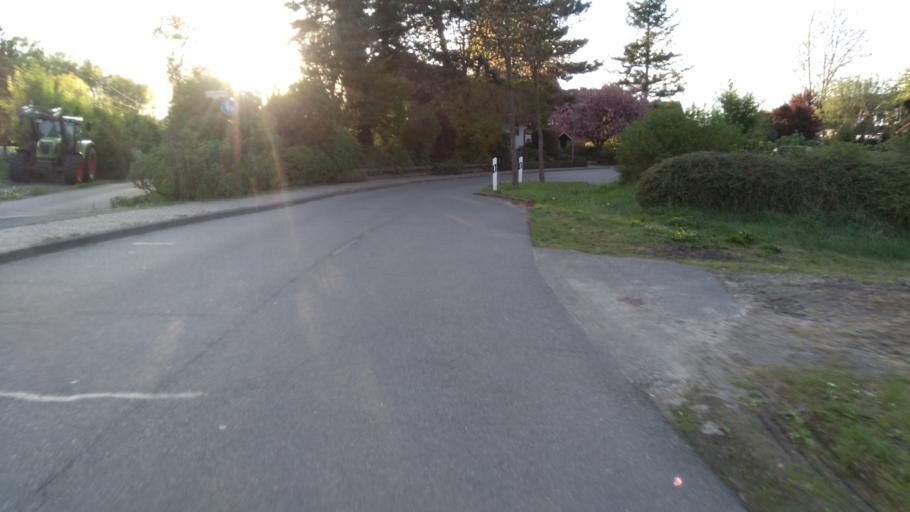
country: DE
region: Lower Saxony
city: Buxtehude
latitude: 53.4736
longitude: 9.6641
